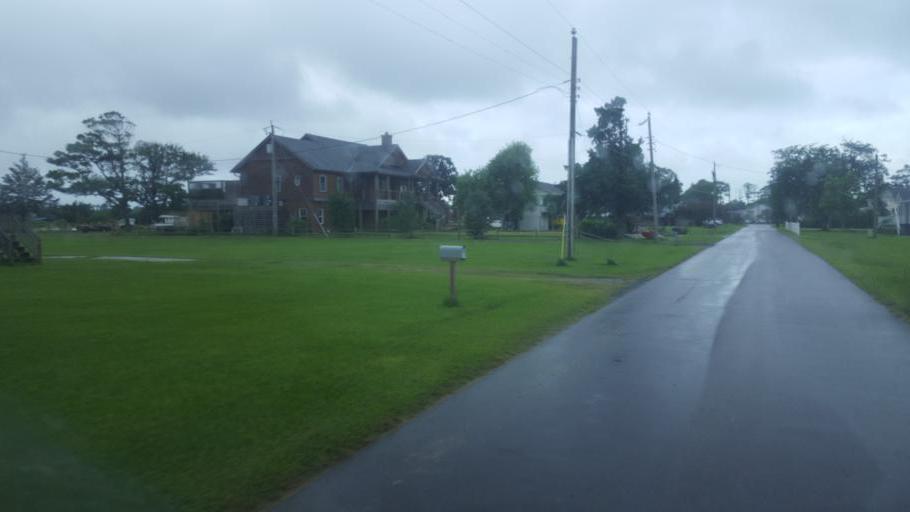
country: US
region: North Carolina
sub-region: Dare County
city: Wanchese
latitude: 35.8382
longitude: -75.6222
